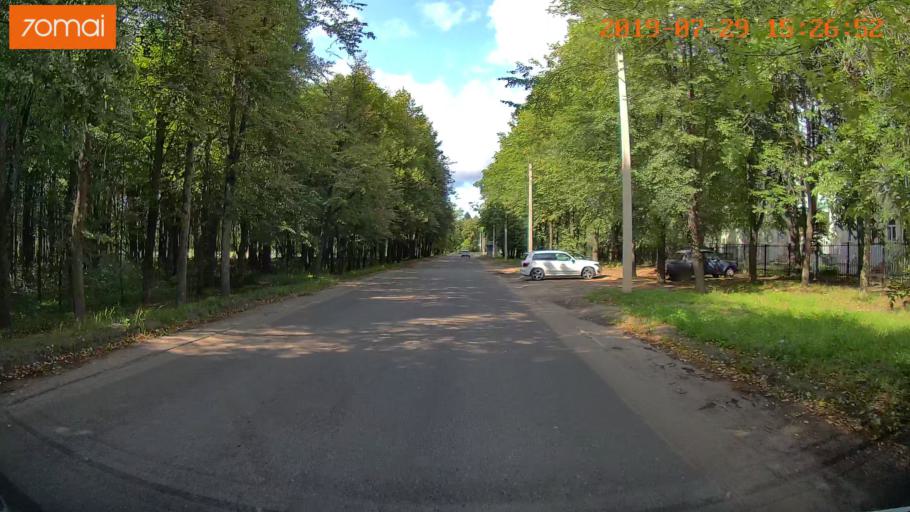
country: RU
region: Ivanovo
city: Bogorodskoye
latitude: 57.0183
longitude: 41.0057
